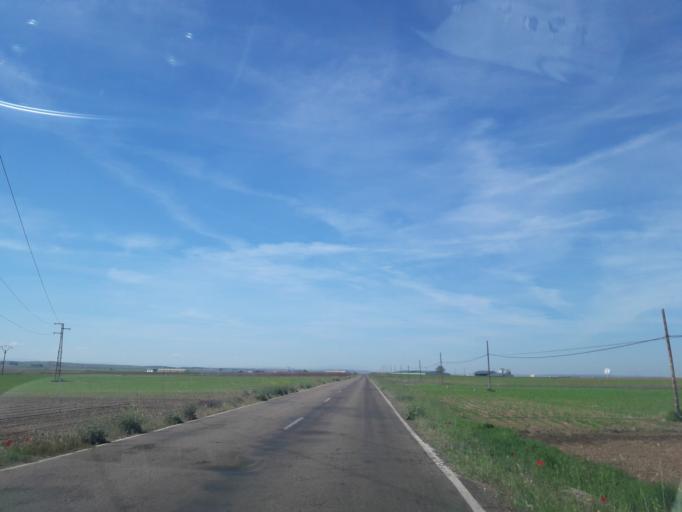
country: ES
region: Castille and Leon
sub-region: Provincia de Salamanca
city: Villoruela
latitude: 40.9985
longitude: -5.4008
